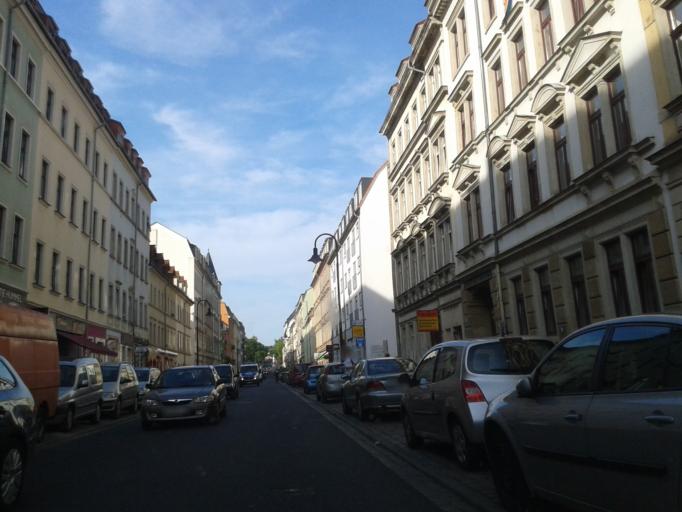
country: DE
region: Saxony
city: Albertstadt
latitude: 51.0723
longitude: 13.7475
